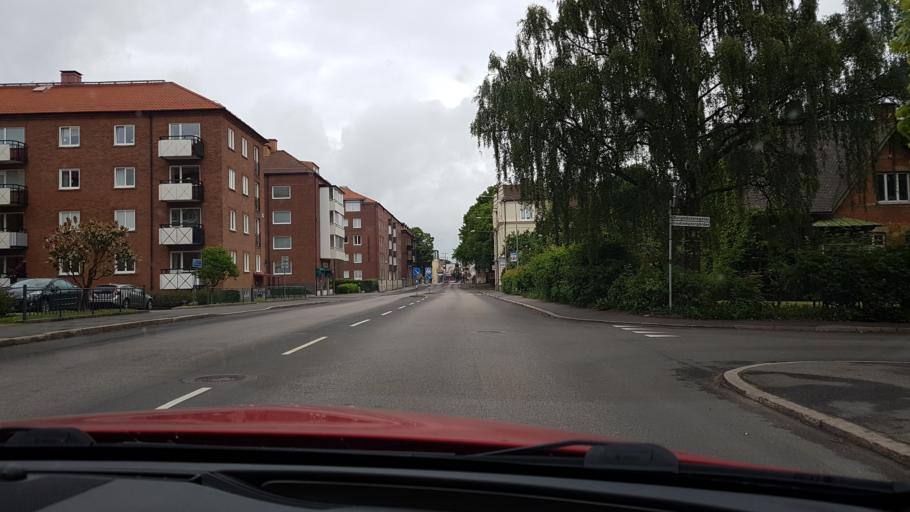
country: SE
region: Vaestra Goetaland
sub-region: Skovde Kommun
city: Skoevde
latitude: 58.3851
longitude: 13.8448
